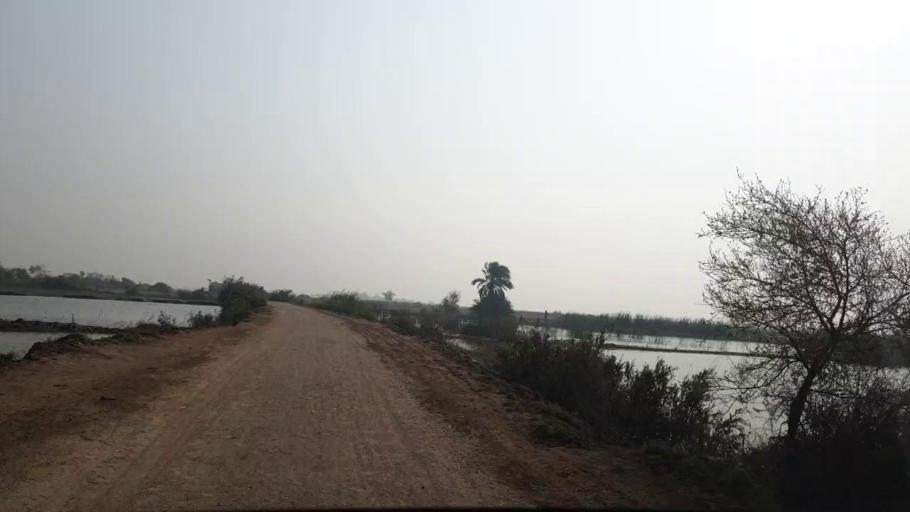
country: PK
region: Sindh
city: Chuhar Jamali
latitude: 24.4861
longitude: 68.0653
